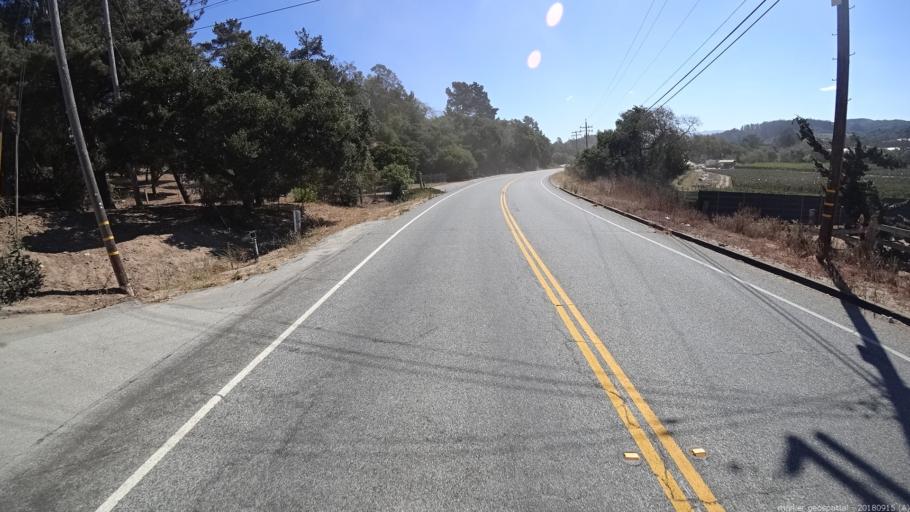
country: US
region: California
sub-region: San Benito County
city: Aromas
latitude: 36.8685
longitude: -121.6727
